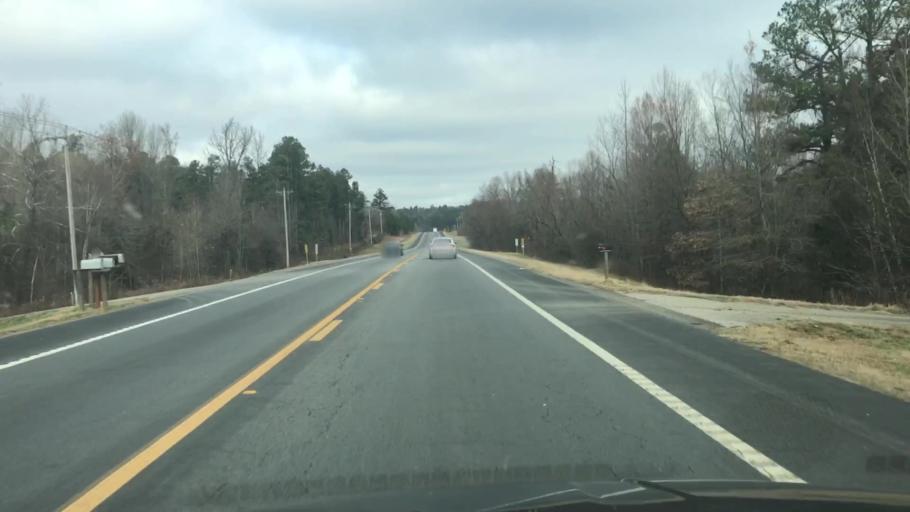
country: US
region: Arkansas
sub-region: Scott County
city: Waldron
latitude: 34.8303
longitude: -94.0411
